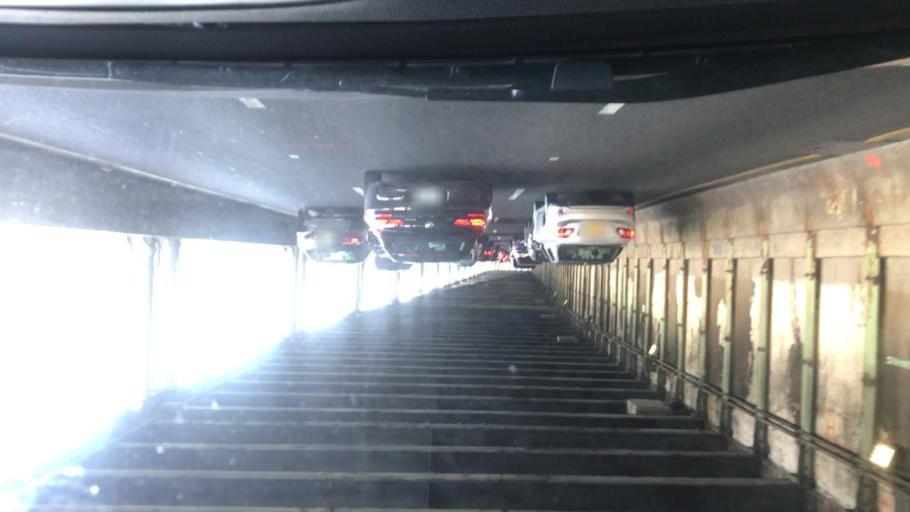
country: US
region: New York
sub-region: New York County
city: Manhattan
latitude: 40.7727
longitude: -73.9452
